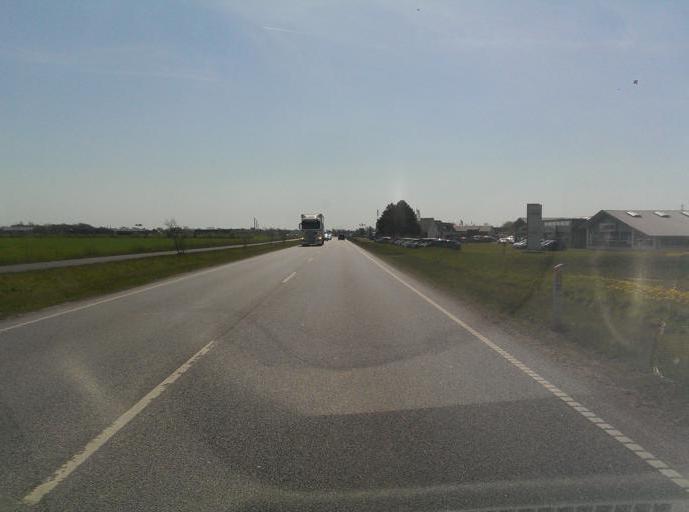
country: DK
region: South Denmark
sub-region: Esbjerg Kommune
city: Ribe
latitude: 55.3571
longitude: 8.7750
